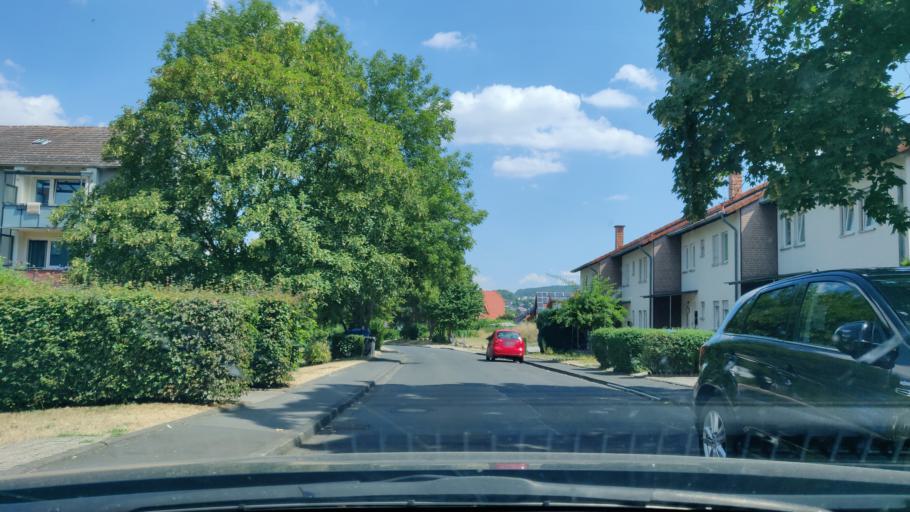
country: DE
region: Hesse
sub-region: Regierungsbezirk Kassel
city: Homberg
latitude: 51.0245
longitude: 9.4092
